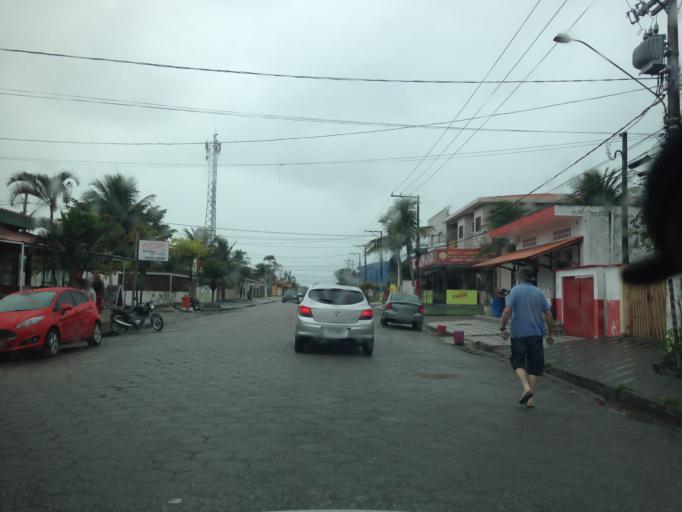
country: BR
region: Sao Paulo
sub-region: Itanhaem
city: Itanhaem
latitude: -24.2196
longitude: -46.8662
